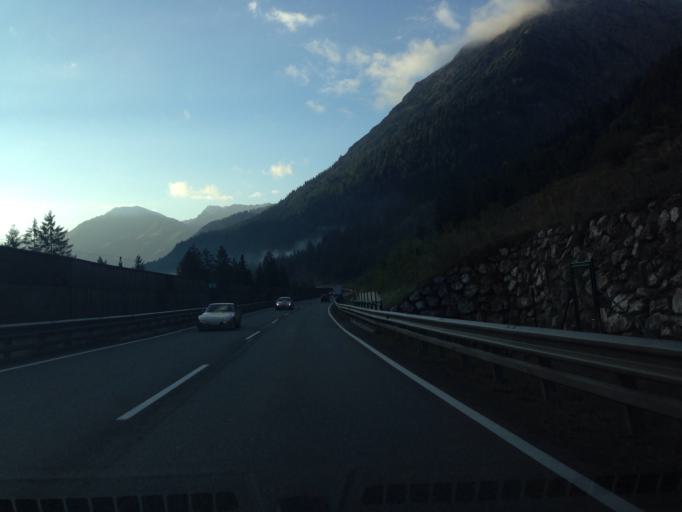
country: AT
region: Tyrol
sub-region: Politischer Bezirk Reutte
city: Heiterwang
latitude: 47.4465
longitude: 10.7379
